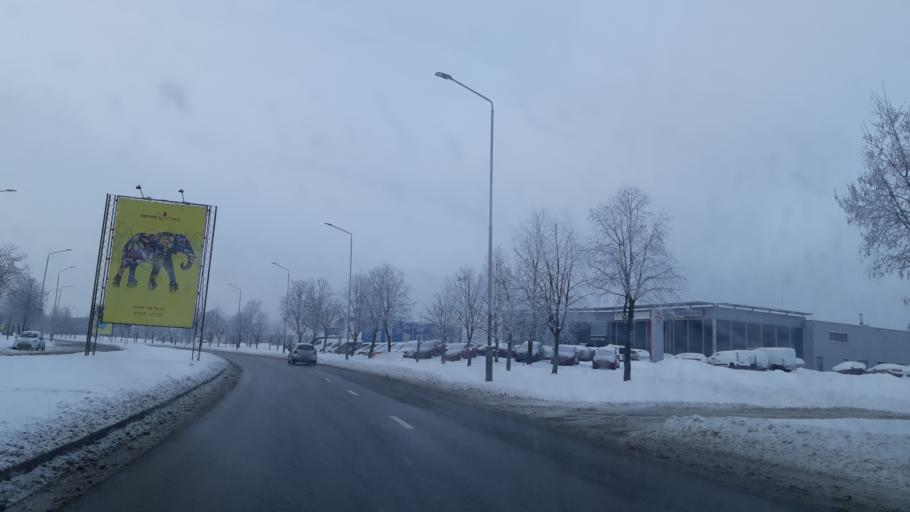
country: LT
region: Kauno apskritis
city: Dainava (Kaunas)
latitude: 54.9302
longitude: 23.9692
